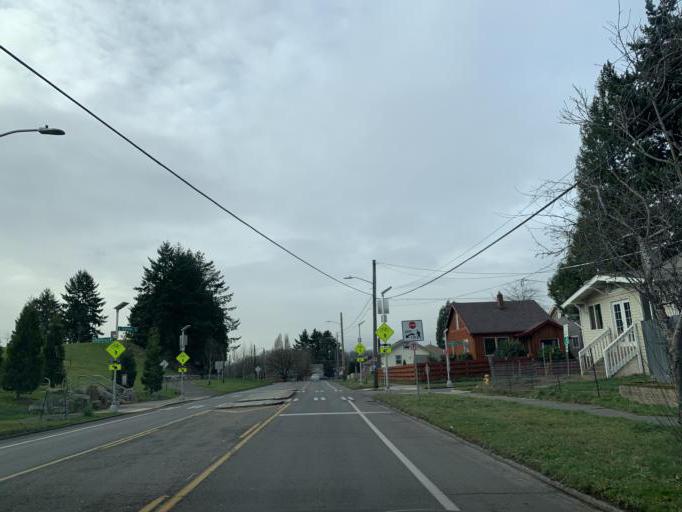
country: US
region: Washington
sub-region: King County
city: Seattle
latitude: 47.5720
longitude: -122.3098
